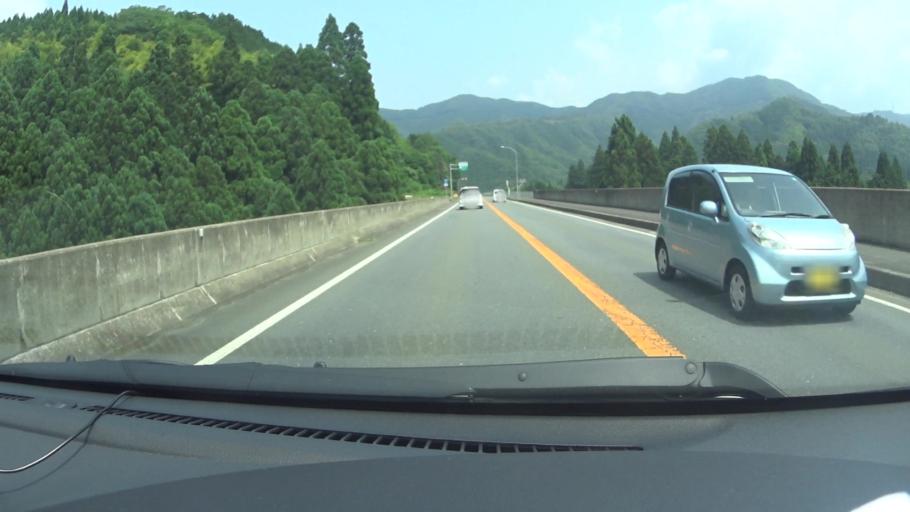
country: JP
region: Kyoto
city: Ayabe
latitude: 35.2702
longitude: 135.3644
